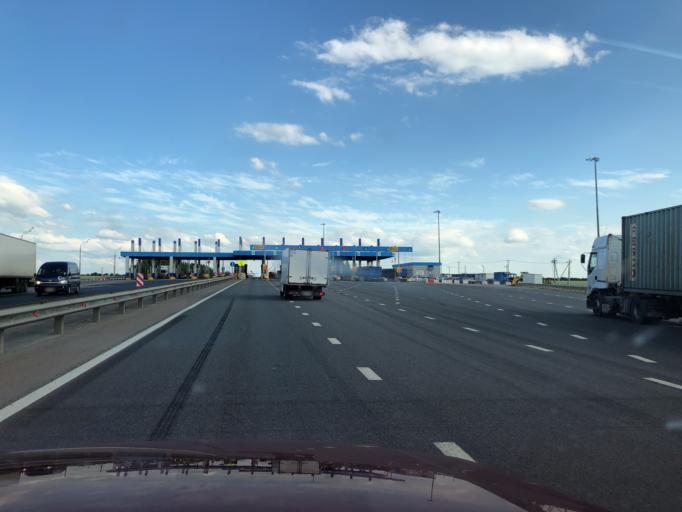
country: RU
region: Lipetsk
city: Zadonsk
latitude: 52.4312
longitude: 38.8232
